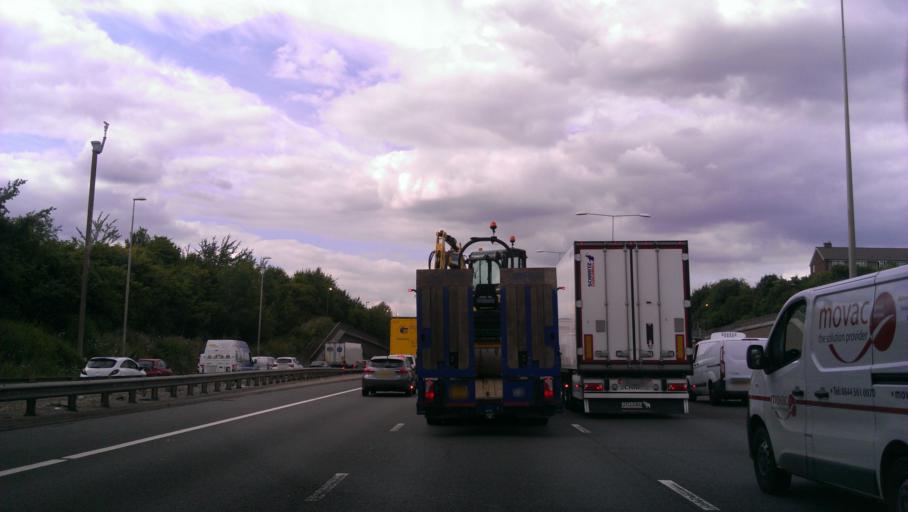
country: GB
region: England
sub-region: Kent
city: Dartford
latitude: 51.4339
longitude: 0.2390
